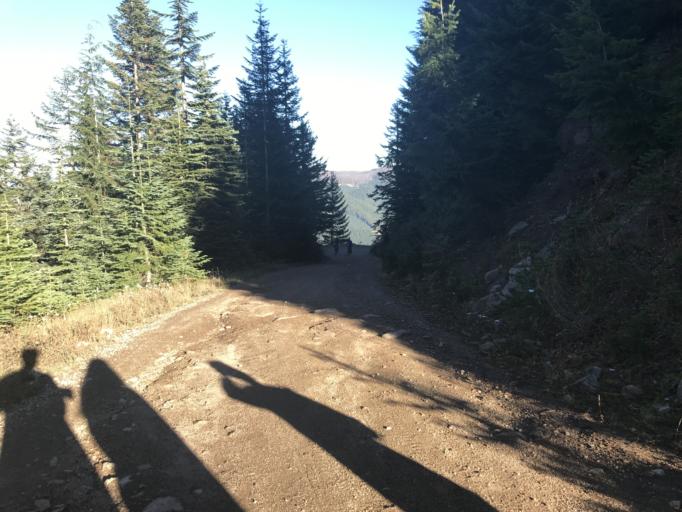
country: US
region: Washington
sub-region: King County
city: Enumclaw
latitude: 47.0427
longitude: -121.5962
